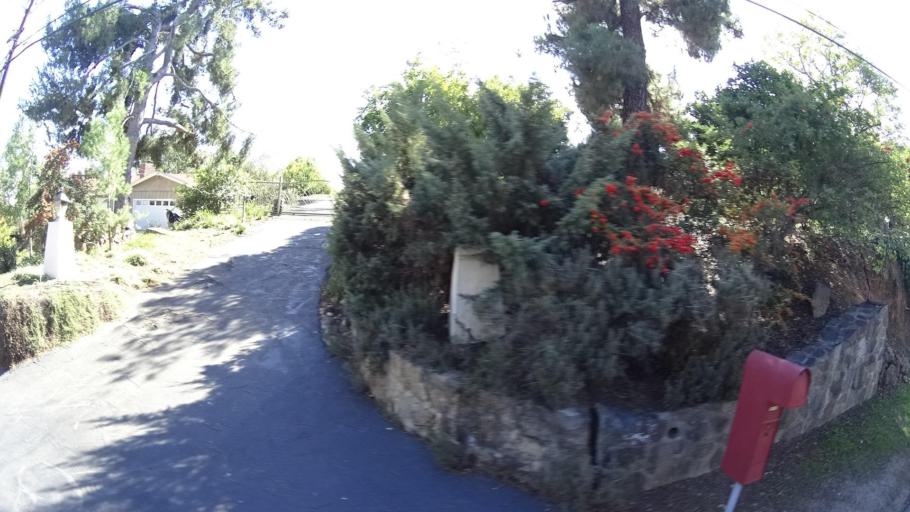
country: US
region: California
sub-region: San Diego County
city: Casa de Oro-Mount Helix
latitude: 32.7654
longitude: -116.9628
